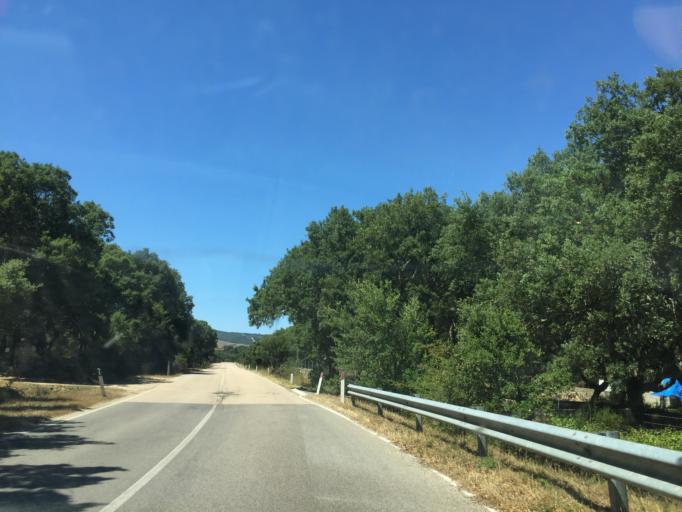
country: IT
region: Sardinia
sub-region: Provincia di Olbia-Tempio
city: Aggius
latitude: 40.9756
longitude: 9.0940
